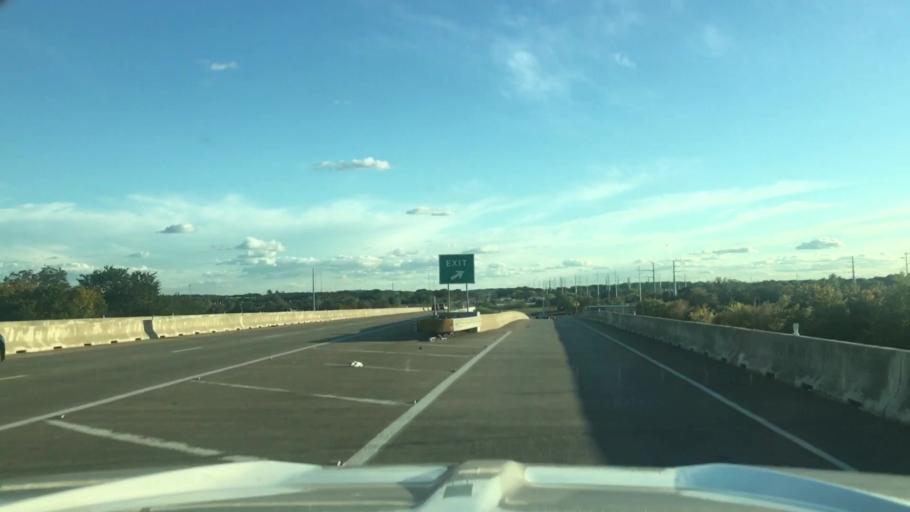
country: US
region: Texas
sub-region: Denton County
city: Denton
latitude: 33.2362
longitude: -97.0900
